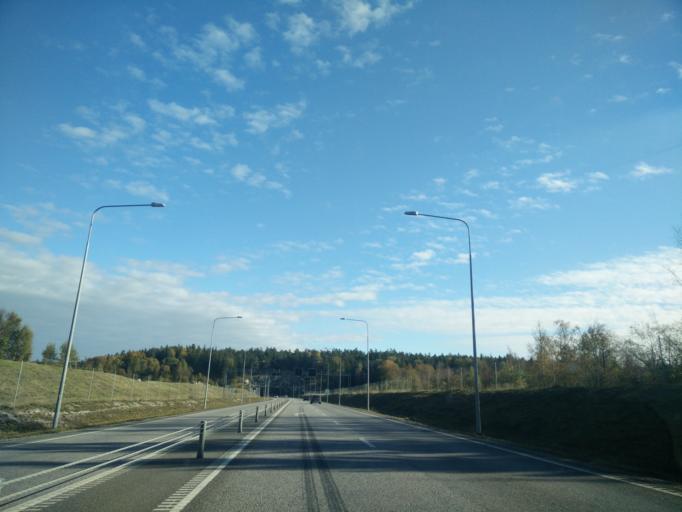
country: SE
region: Stockholm
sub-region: Taby Kommun
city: Taby
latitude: 59.4801
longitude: 18.0802
